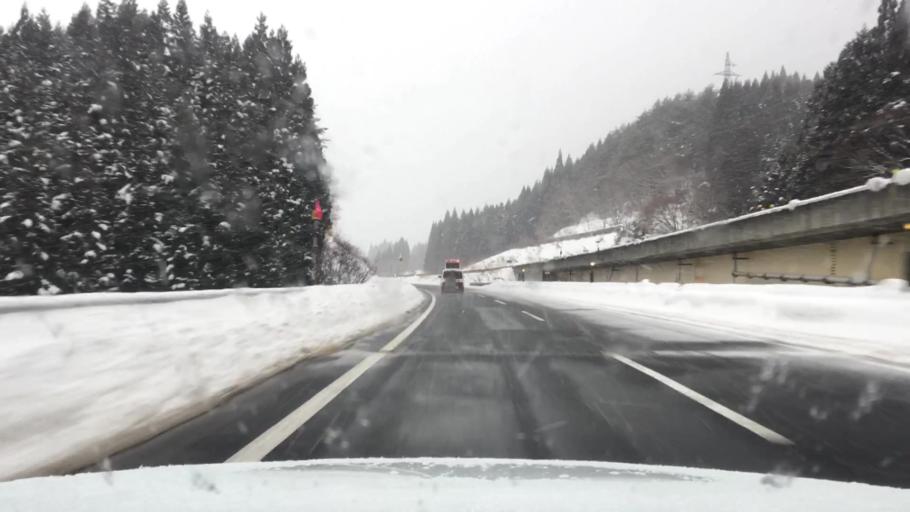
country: JP
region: Akita
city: Hanawa
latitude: 40.1452
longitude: 140.8083
